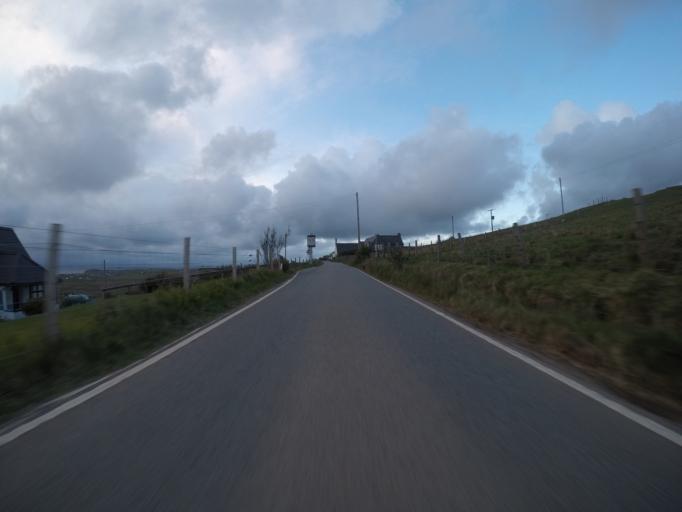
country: GB
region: Scotland
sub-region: Highland
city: Portree
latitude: 57.6344
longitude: -6.3767
